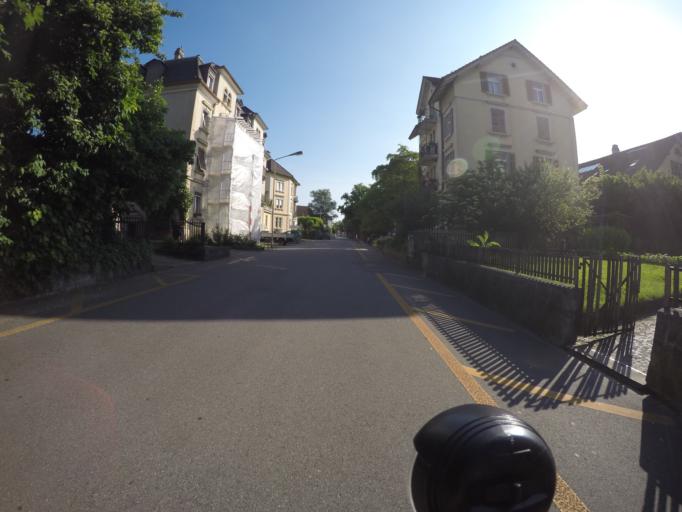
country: CH
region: Zurich
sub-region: Bezirk Winterthur
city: Toess (Kreis 4) / Eichliacker
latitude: 47.4875
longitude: 8.7087
